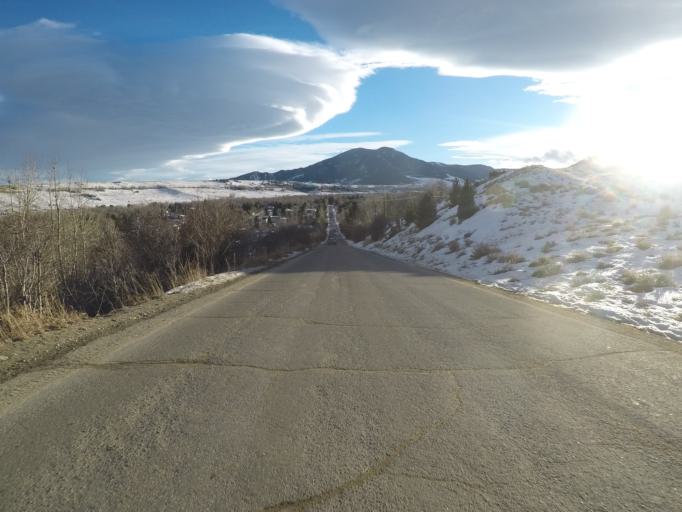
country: US
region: Montana
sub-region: Carbon County
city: Red Lodge
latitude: 45.1826
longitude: -109.2548
